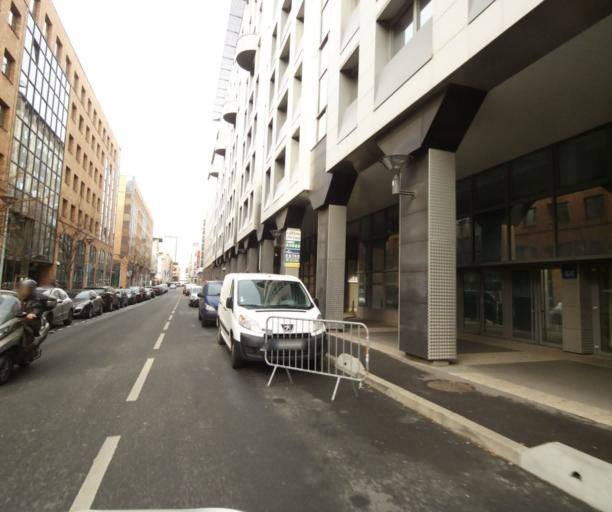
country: FR
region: Ile-de-France
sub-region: Departement des Hauts-de-Seine
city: La Defense
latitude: 48.8947
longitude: 2.2252
